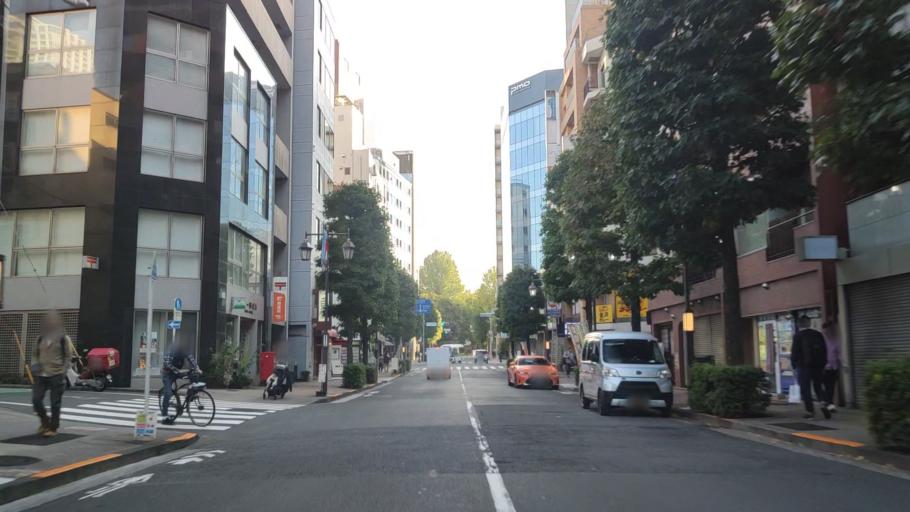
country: JP
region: Tokyo
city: Tokyo
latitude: 35.6897
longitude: 139.7099
